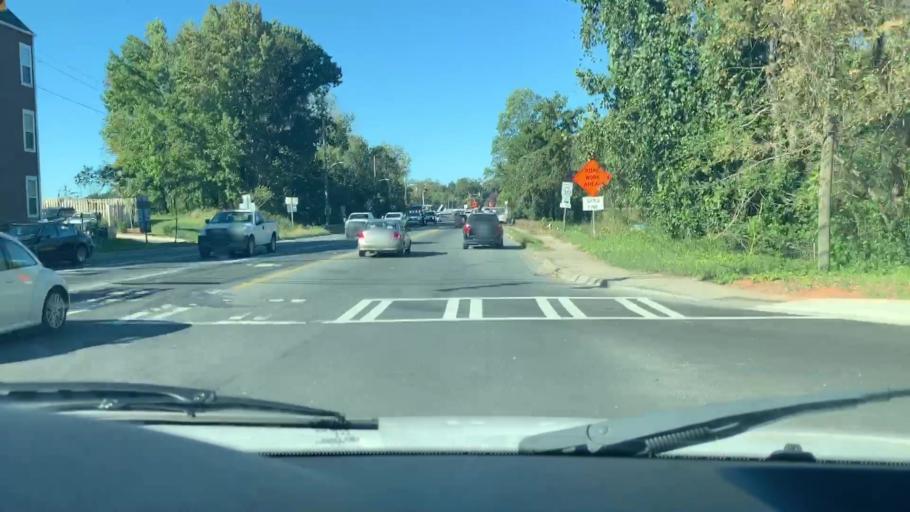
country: US
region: North Carolina
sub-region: Mecklenburg County
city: Charlotte
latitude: 35.2613
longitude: -80.8371
